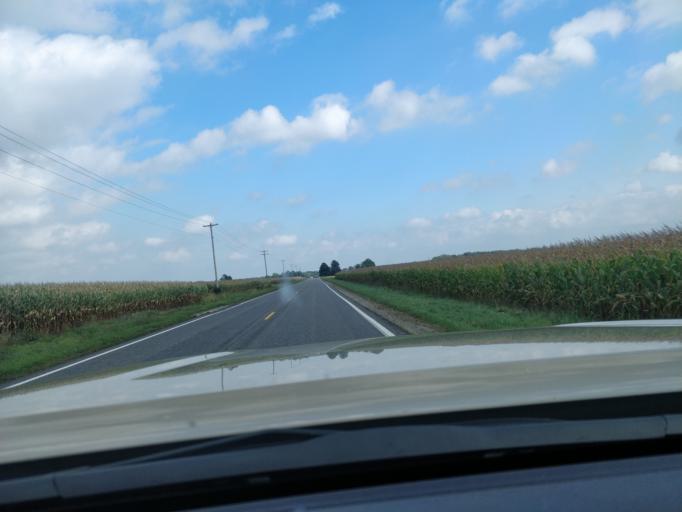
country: US
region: Michigan
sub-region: Ionia County
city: Saranac
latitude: 42.8862
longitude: -85.2309
